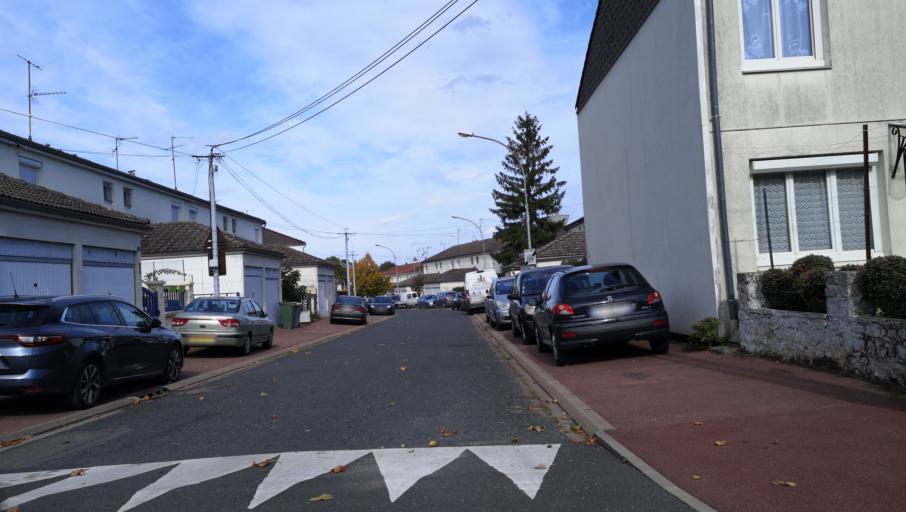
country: FR
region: Centre
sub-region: Departement du Loiret
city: Saint-Jean-de-la-Ruelle
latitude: 47.9242
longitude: 1.8809
